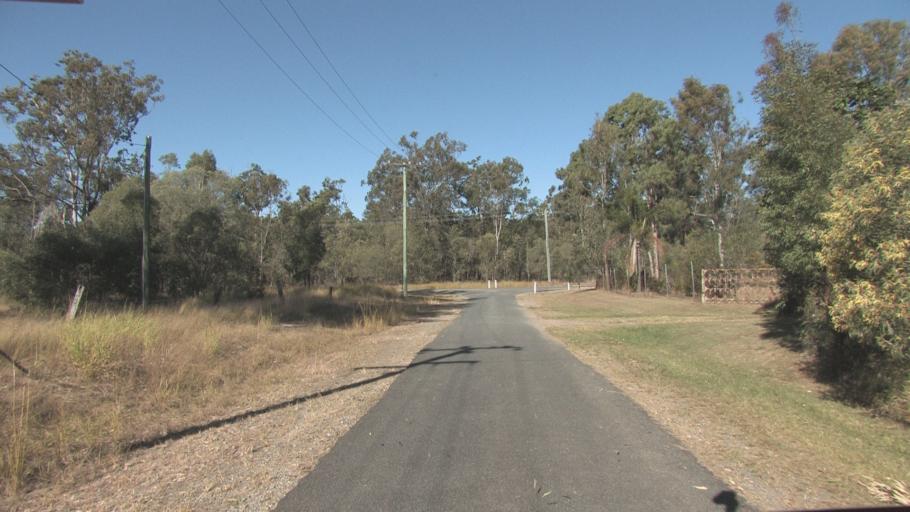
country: AU
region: Queensland
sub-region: Ipswich
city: Springfield Lakes
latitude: -27.7280
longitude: 152.9523
